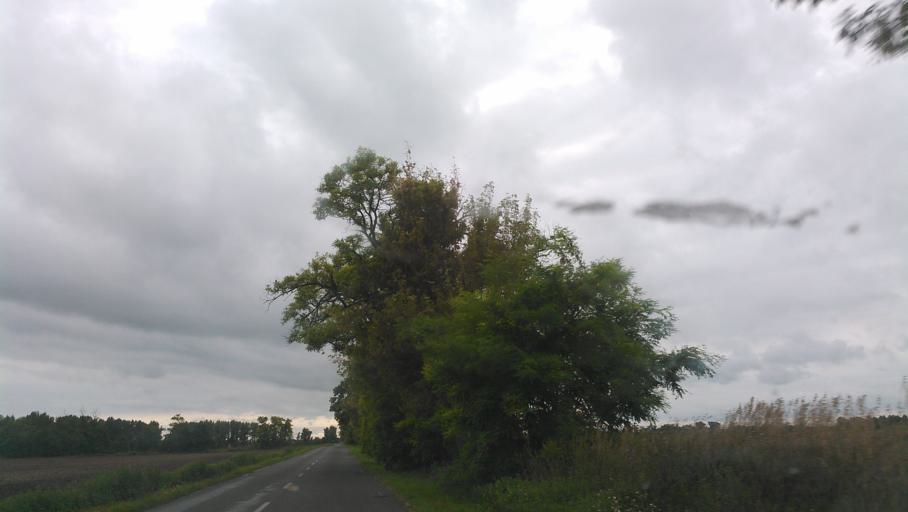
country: SK
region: Trnavsky
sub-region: Okres Dunajska Streda
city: Velky Meder
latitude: 47.9182
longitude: 17.7462
